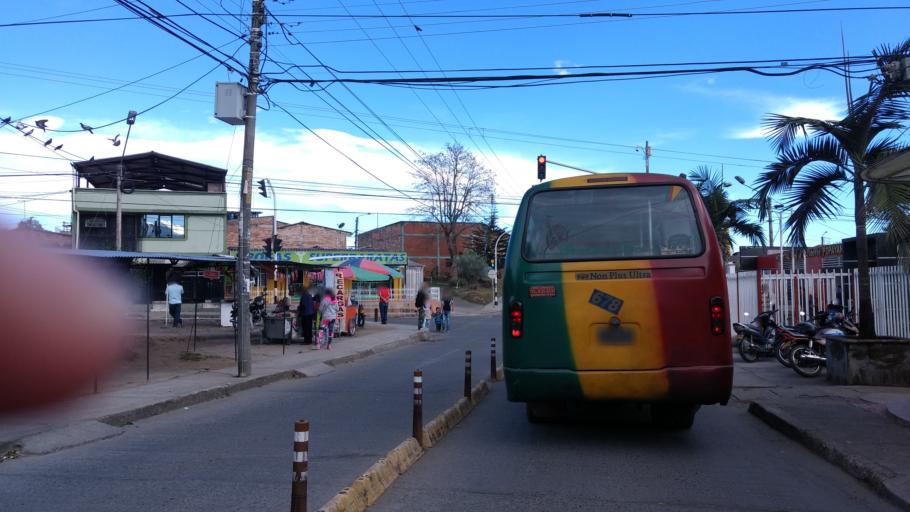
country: CO
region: Cauca
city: Popayan
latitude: 2.4564
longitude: -76.6325
